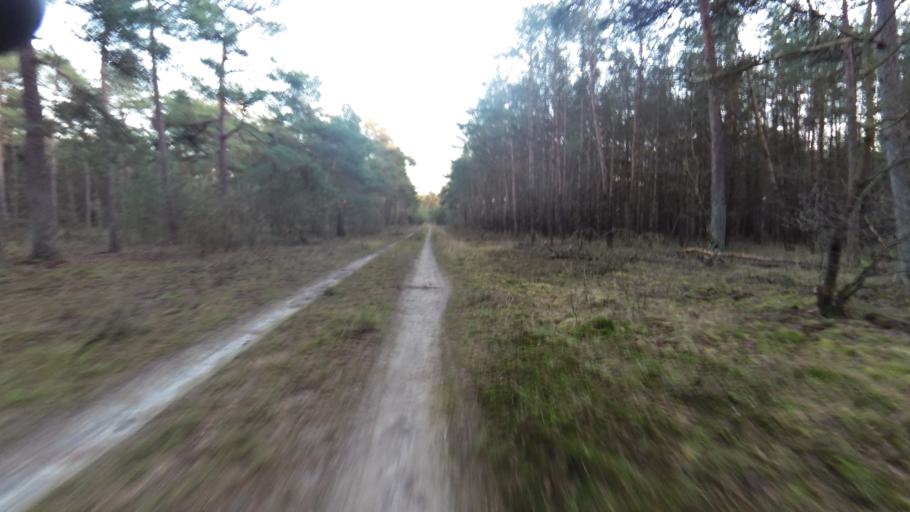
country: NL
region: Gelderland
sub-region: Gemeente Apeldoorn
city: Uddel
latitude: 52.1989
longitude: 5.7958
